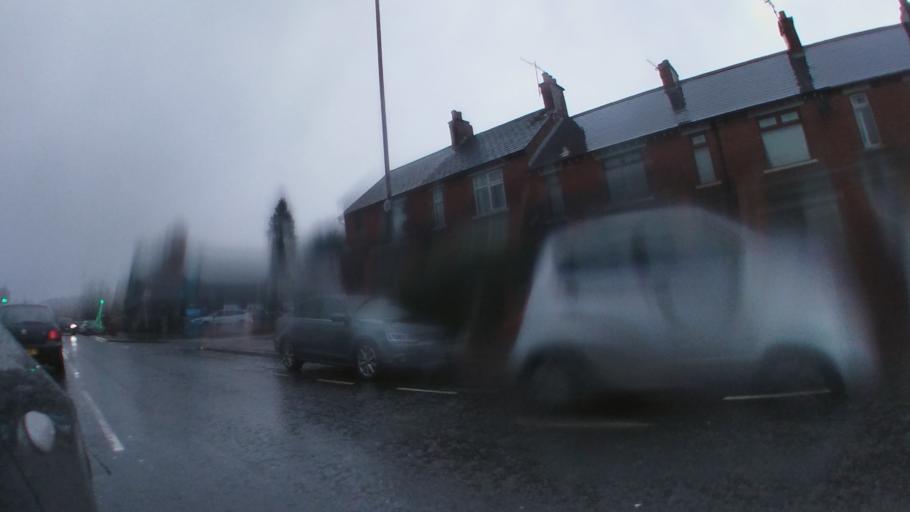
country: GB
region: Northern Ireland
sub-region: City of Belfast
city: Belfast
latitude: 54.6218
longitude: -5.9557
